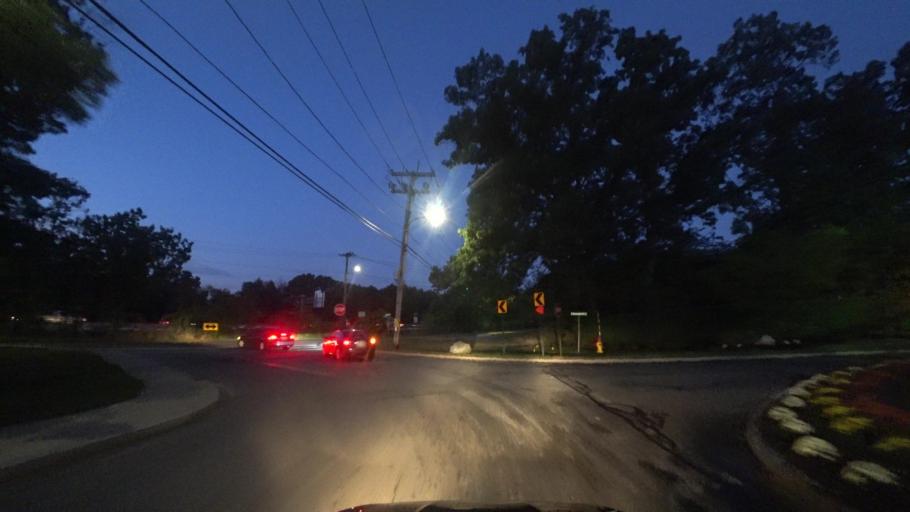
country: US
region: Massachusetts
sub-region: Middlesex County
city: Woburn
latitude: 42.4985
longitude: -71.1679
